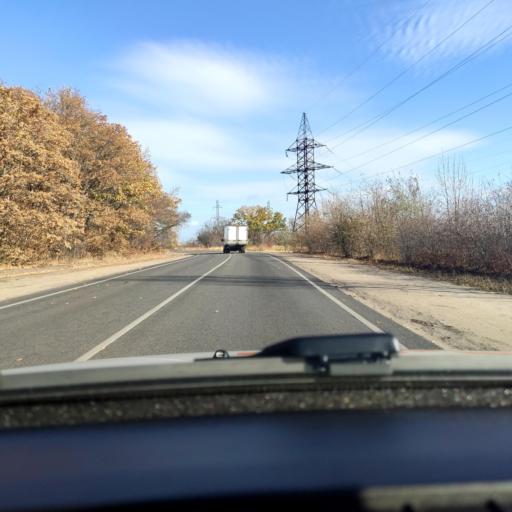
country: RU
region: Voronezj
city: Shilovo
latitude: 51.5606
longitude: 39.1390
